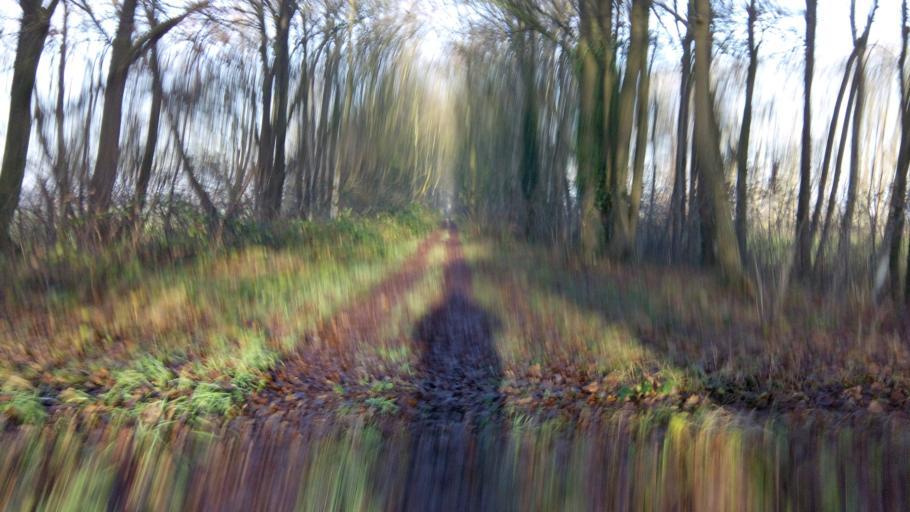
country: NL
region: Utrecht
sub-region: Gemeente Utrechtse Heuvelrug
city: Overberg
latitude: 52.0657
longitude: 5.4630
